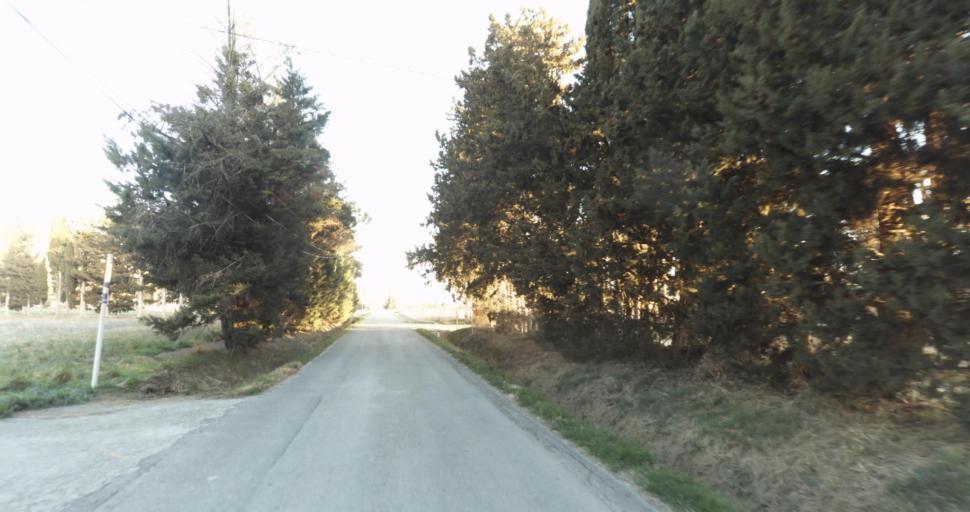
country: FR
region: Provence-Alpes-Cote d'Azur
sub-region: Departement des Bouches-du-Rhone
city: Barbentane
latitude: 43.8889
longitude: 4.7724
